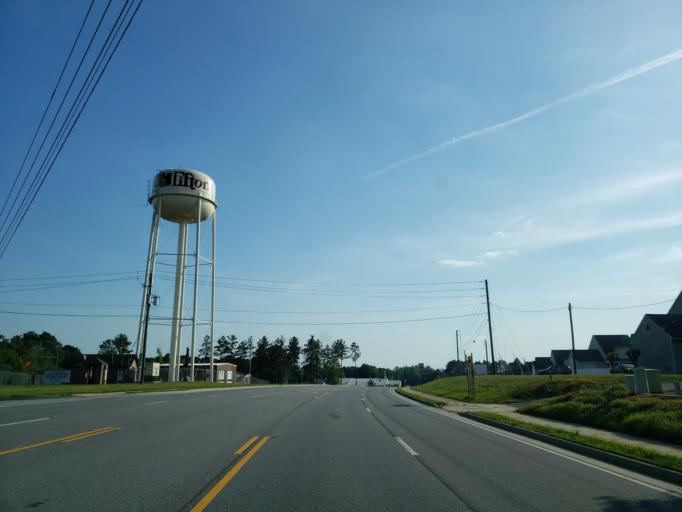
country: US
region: Georgia
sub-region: Tift County
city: Tifton
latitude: 31.4737
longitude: -83.5433
